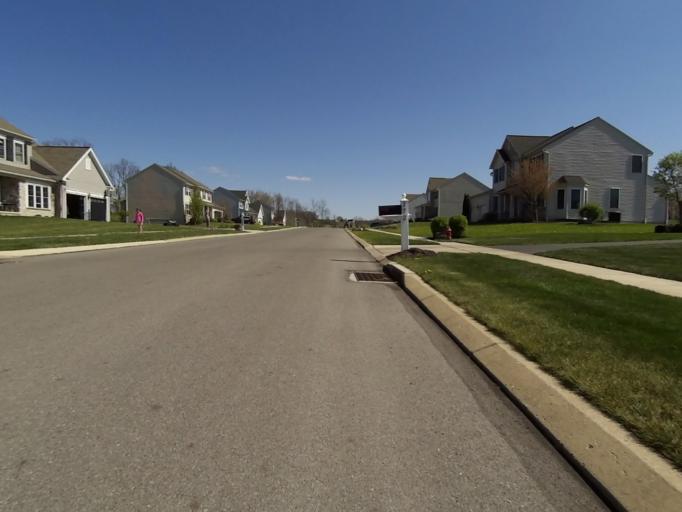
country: US
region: Pennsylvania
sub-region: Centre County
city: Houserville
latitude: 40.8824
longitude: -77.8327
